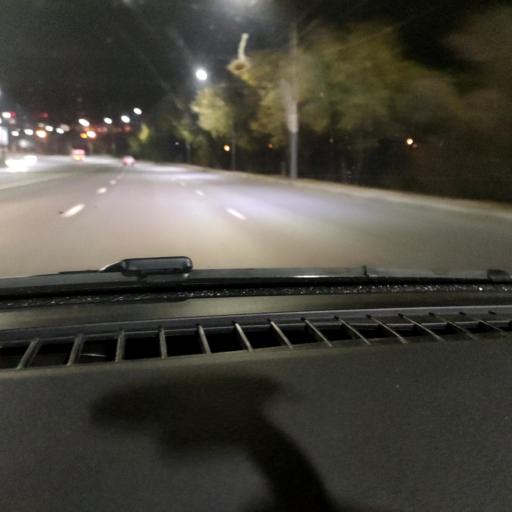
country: RU
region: Voronezj
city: Voronezh
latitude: 51.6383
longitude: 39.2067
